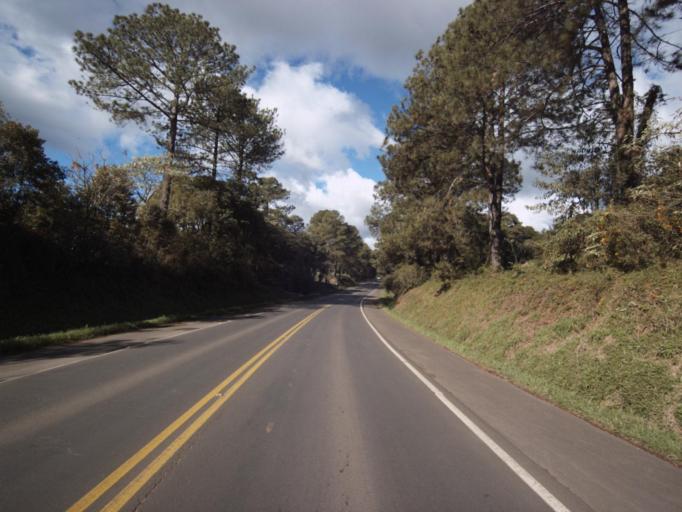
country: BR
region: Santa Catarina
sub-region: Joacaba
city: Joacaba
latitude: -27.0165
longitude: -51.7339
